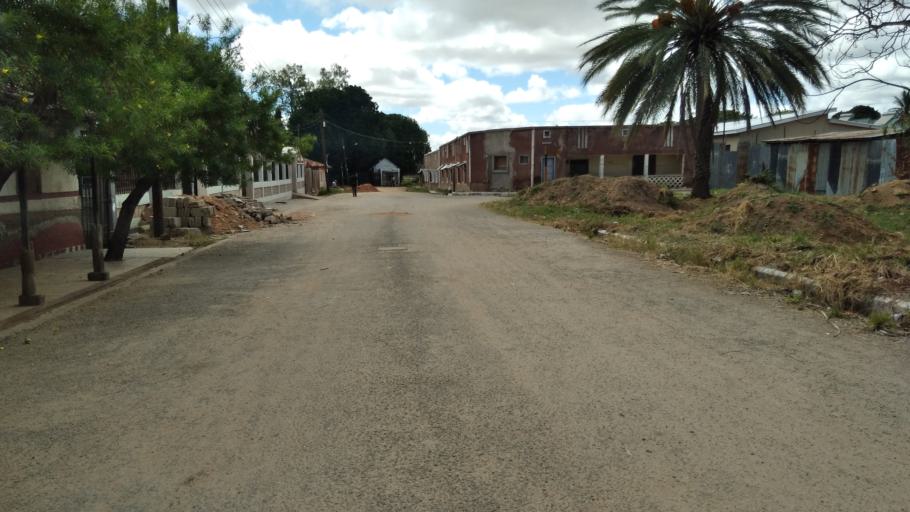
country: TZ
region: Dodoma
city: Dodoma
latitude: -6.1719
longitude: 35.7520
